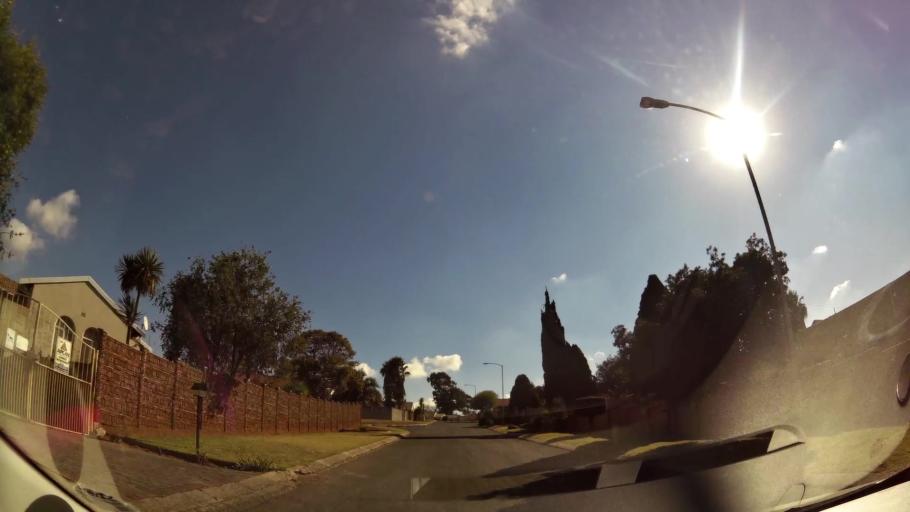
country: ZA
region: Gauteng
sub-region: City of Johannesburg Metropolitan Municipality
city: Roodepoort
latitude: -26.1476
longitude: 27.8369
